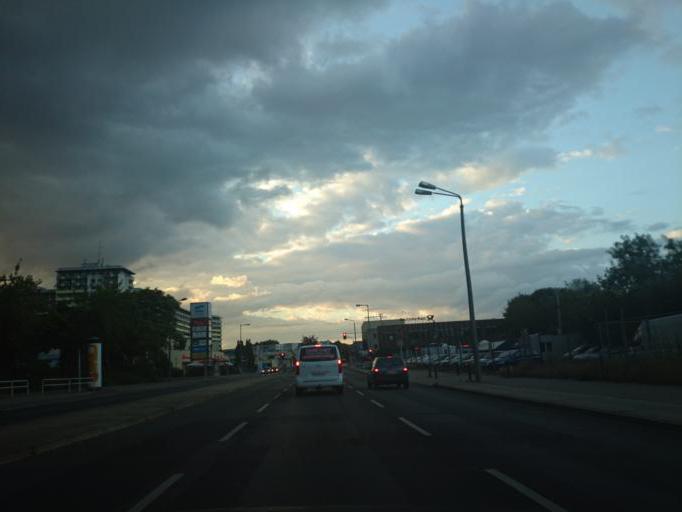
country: DE
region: Berlin
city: Kaulsdorf
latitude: 52.5199
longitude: 13.5884
